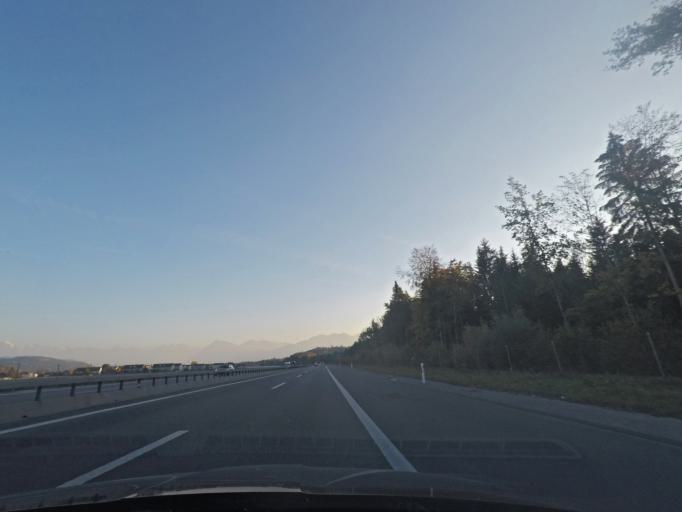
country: CH
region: Bern
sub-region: Bern-Mittelland District
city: Niederwichtrach
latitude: 46.8450
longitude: 7.5593
